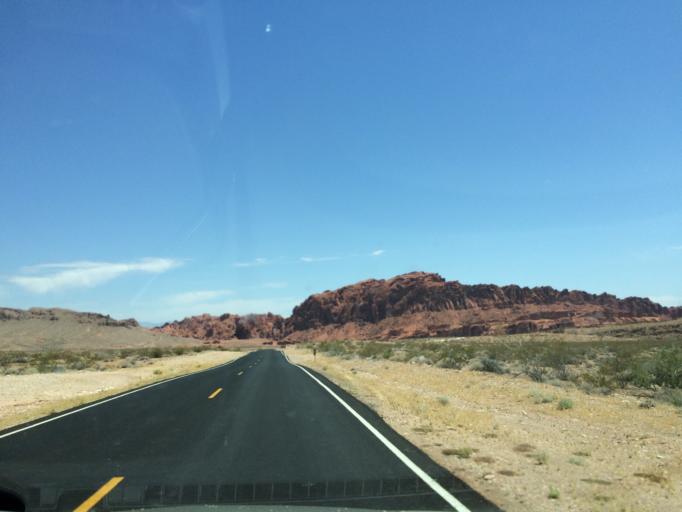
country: US
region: Nevada
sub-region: Clark County
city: Moapa Valley
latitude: 36.4183
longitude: -114.5454
